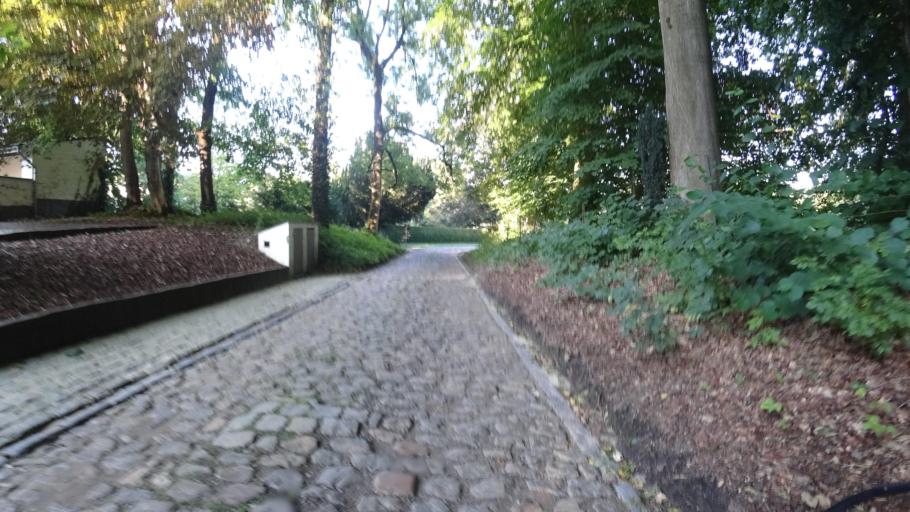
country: BE
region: Wallonia
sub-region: Province du Brabant Wallon
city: Mont-Saint-Guibert
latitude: 50.6317
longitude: 4.6138
